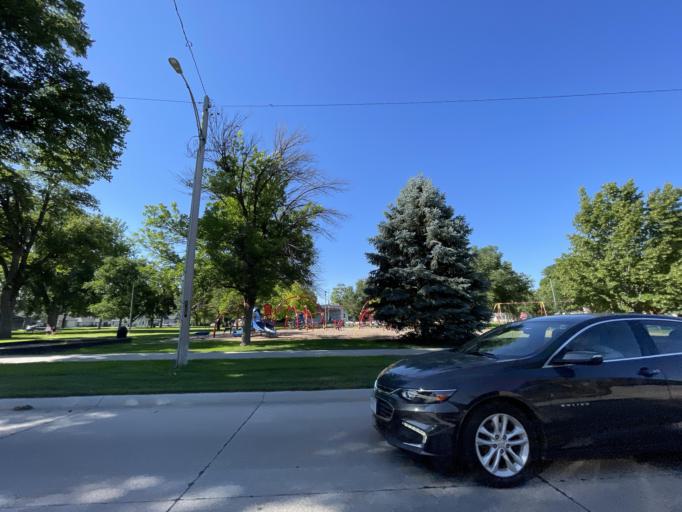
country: US
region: Nebraska
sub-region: Red Willow County
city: McCook
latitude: 40.2047
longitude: -100.6250
